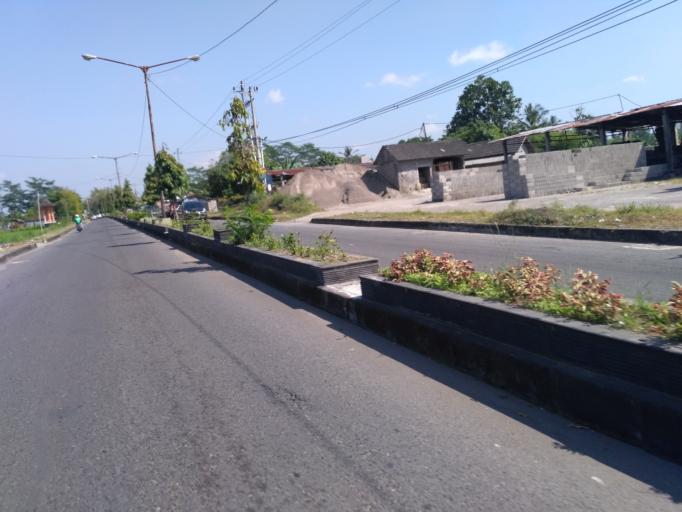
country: ID
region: Daerah Istimewa Yogyakarta
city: Depok
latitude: -7.7513
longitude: 110.4323
